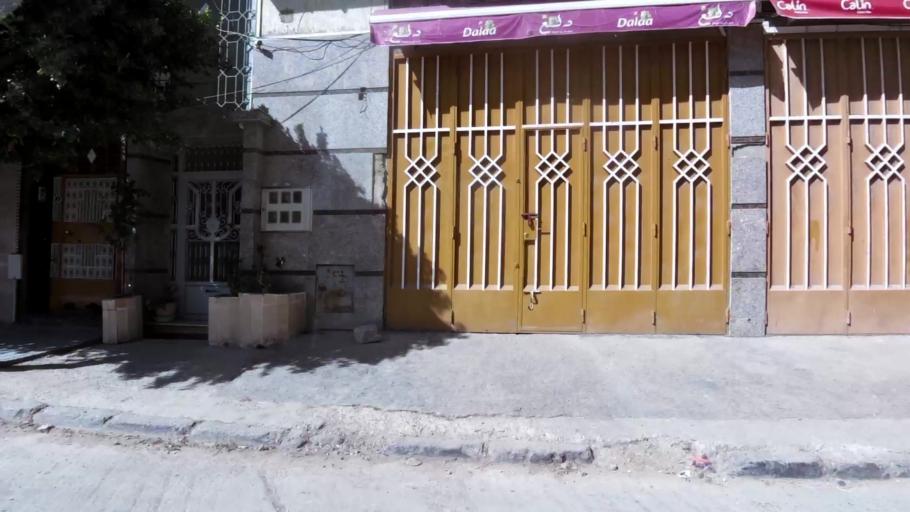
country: MA
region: Tanger-Tetouan
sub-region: Tanger-Assilah
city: Tangier
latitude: 35.7514
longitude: -5.8043
